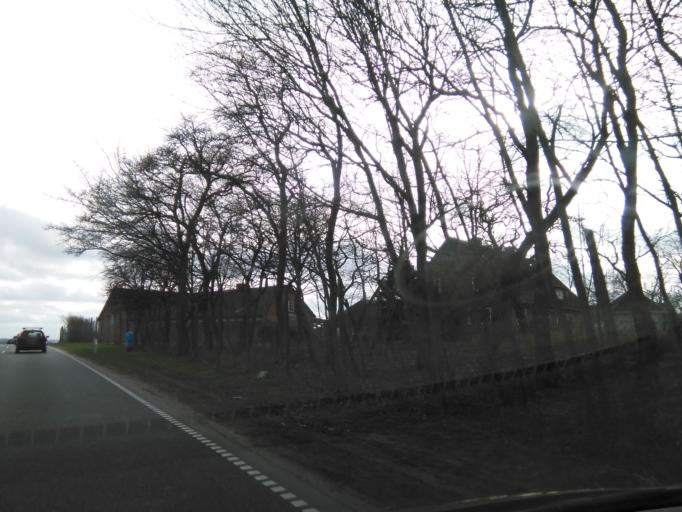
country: DK
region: Central Jutland
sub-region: Arhus Kommune
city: Stavtrup
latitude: 56.1790
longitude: 10.0974
